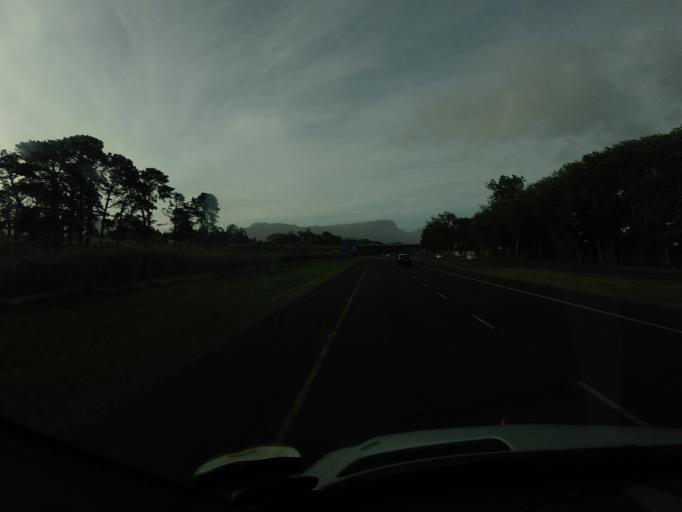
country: ZA
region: Western Cape
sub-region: City of Cape Town
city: Bergvliet
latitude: -34.0470
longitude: 18.4446
